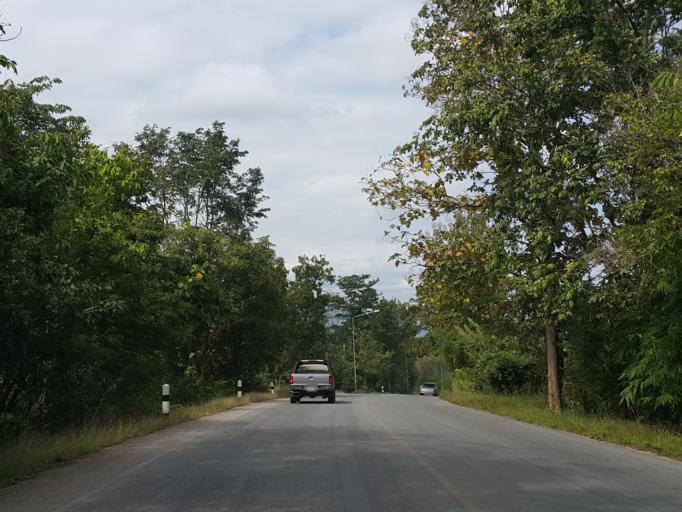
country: TH
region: Lampang
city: Lampang
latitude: 18.3948
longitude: 99.4550
